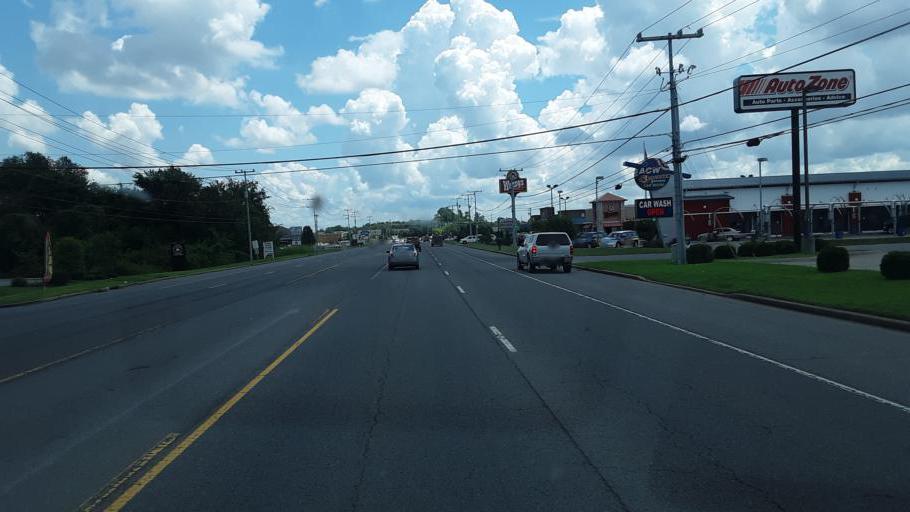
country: US
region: Tennessee
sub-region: Montgomery County
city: Clarksville
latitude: 36.6257
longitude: -87.3245
